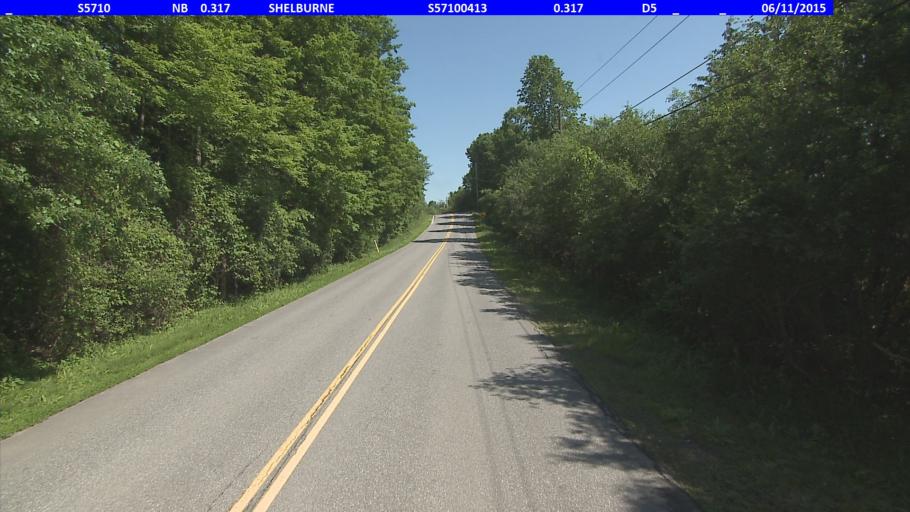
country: US
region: Vermont
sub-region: Chittenden County
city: Hinesburg
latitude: 44.3692
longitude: -73.1808
